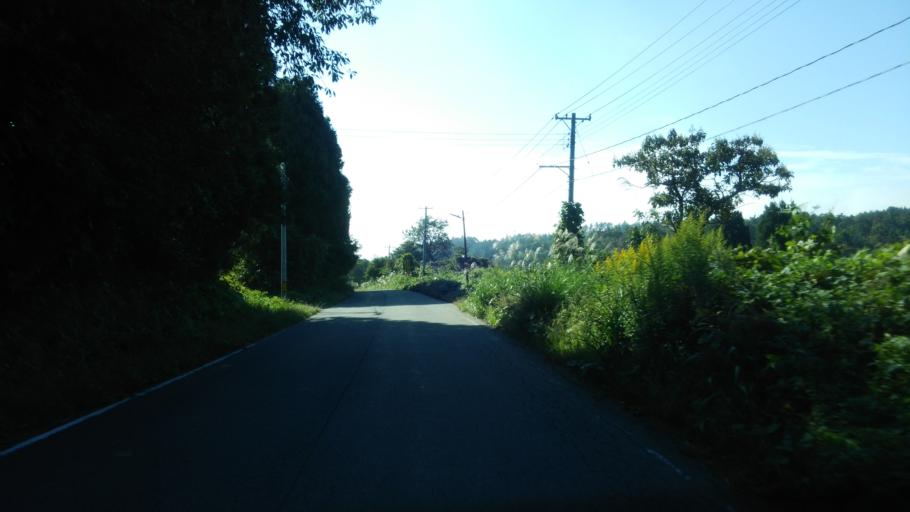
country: JP
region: Fukushima
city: Kitakata
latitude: 37.5908
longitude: 139.9447
